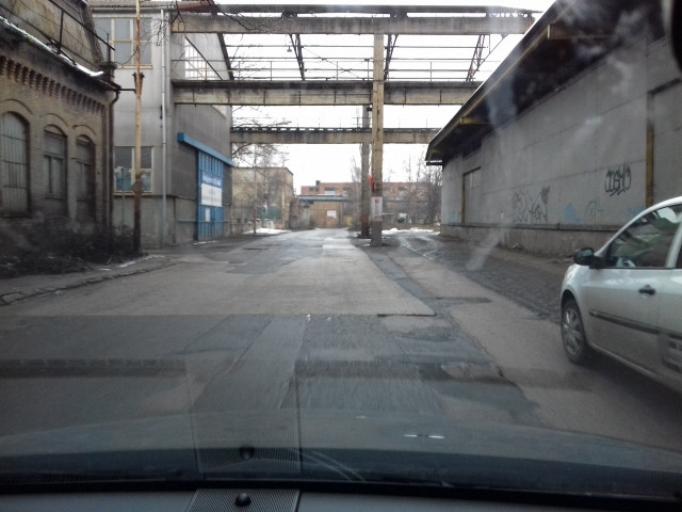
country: HU
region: Budapest
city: Budapest XXI. keruelet
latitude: 47.4265
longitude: 19.0568
